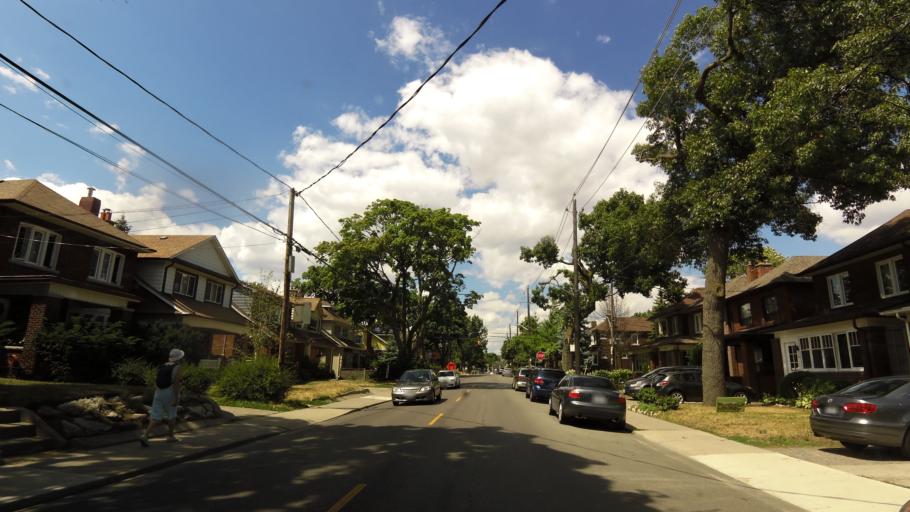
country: CA
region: Ontario
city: Toronto
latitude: 43.6473
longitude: -79.4792
